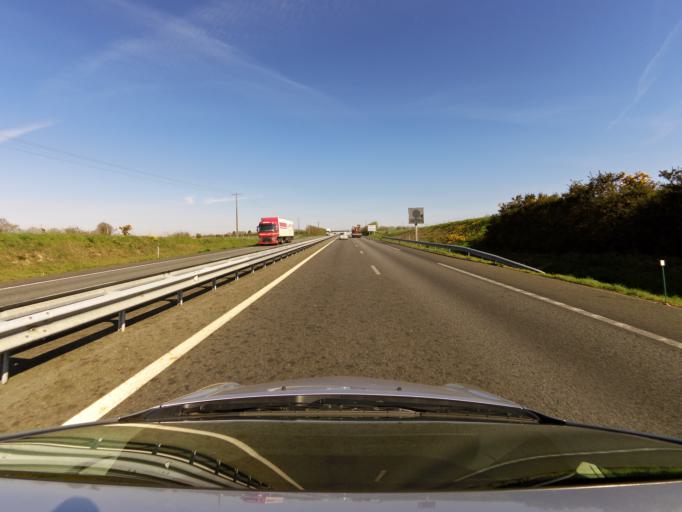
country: FR
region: Brittany
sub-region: Departement d'Ille-et-Vilaine
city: Plelan-le-Grand
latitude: 47.9655
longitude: -2.0941
